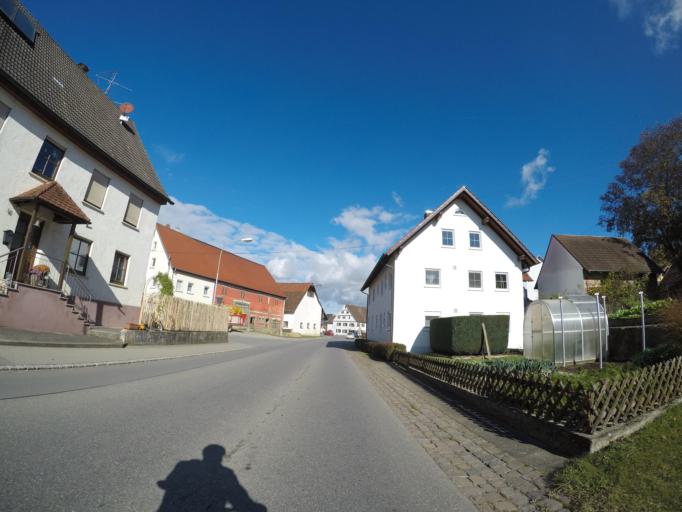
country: DE
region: Baden-Wuerttemberg
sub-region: Tuebingen Region
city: Grundsheim
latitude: 48.1479
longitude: 9.6663
